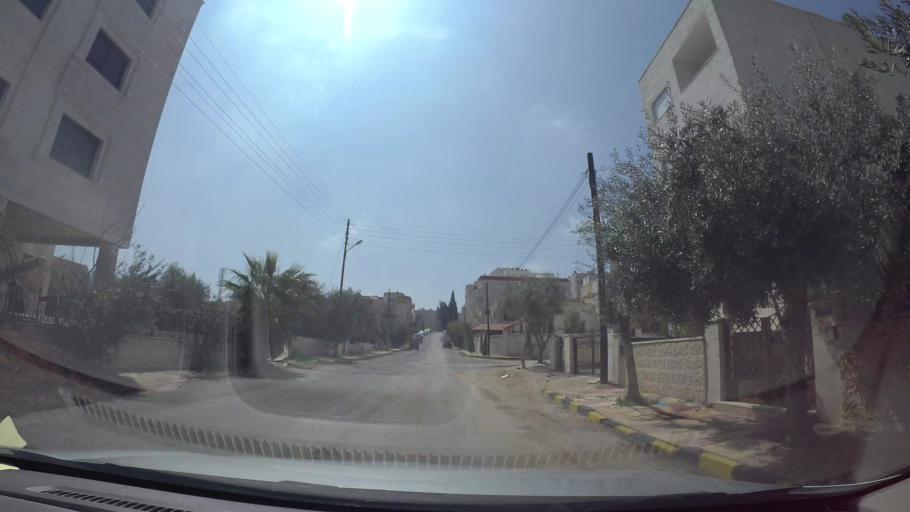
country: JO
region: Amman
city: Al Bunayyat ash Shamaliyah
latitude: 31.8988
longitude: 35.8885
